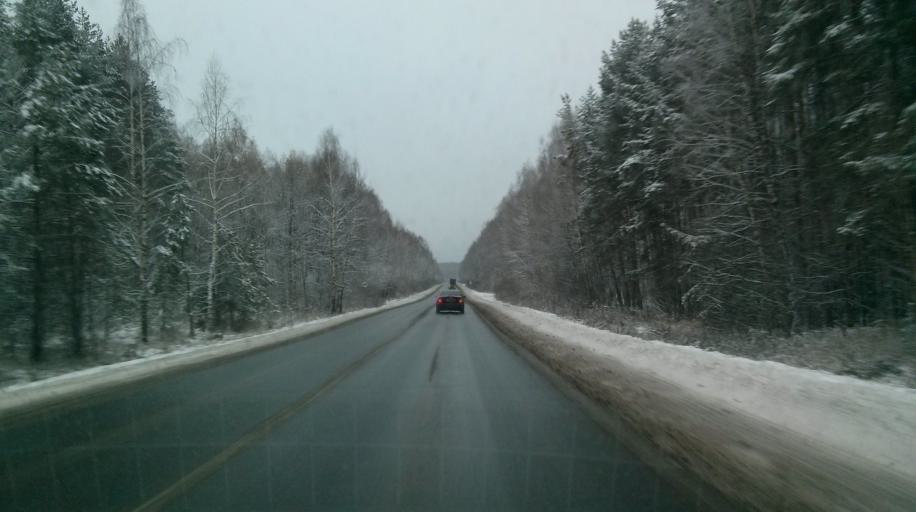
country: RU
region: Nizjnij Novgorod
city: Vorsma
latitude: 56.0218
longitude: 43.3526
